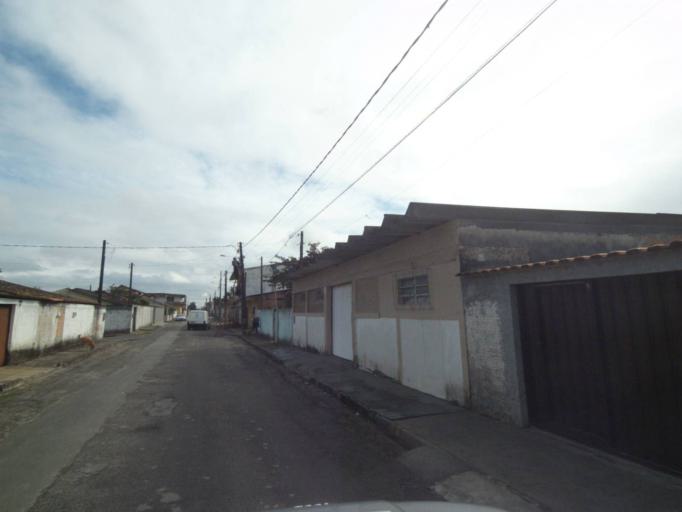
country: BR
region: Parana
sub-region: Paranagua
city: Paranagua
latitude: -25.5679
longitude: -48.5594
